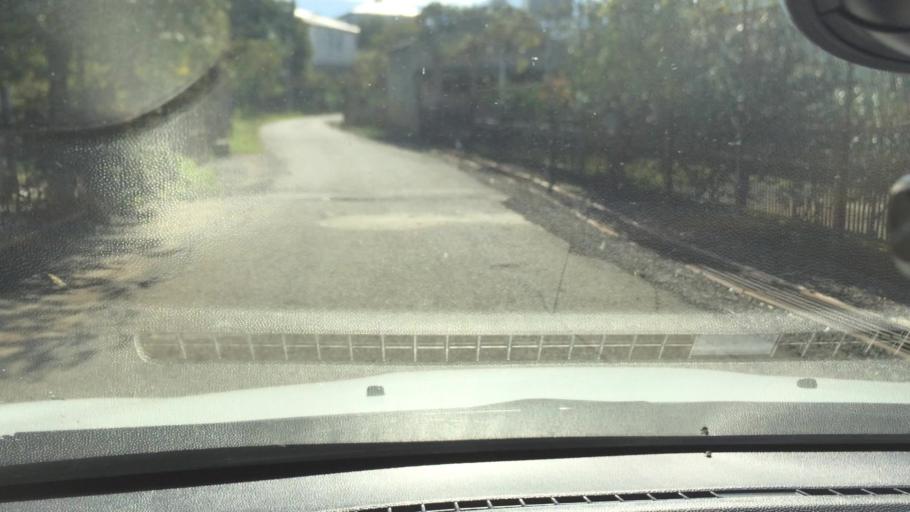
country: GE
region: Ajaria
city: Kobuleti
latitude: 41.8134
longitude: 41.8240
